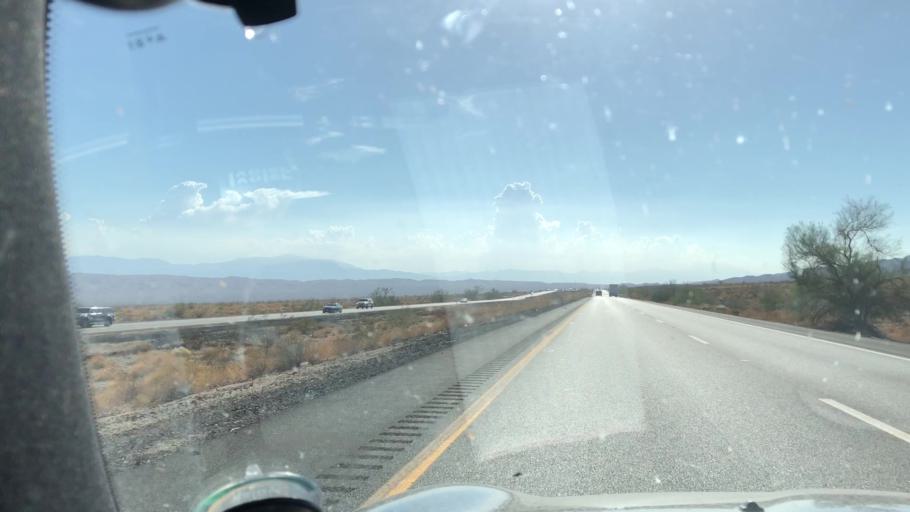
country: US
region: California
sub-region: Riverside County
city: Mecca
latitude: 33.6630
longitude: -115.8492
